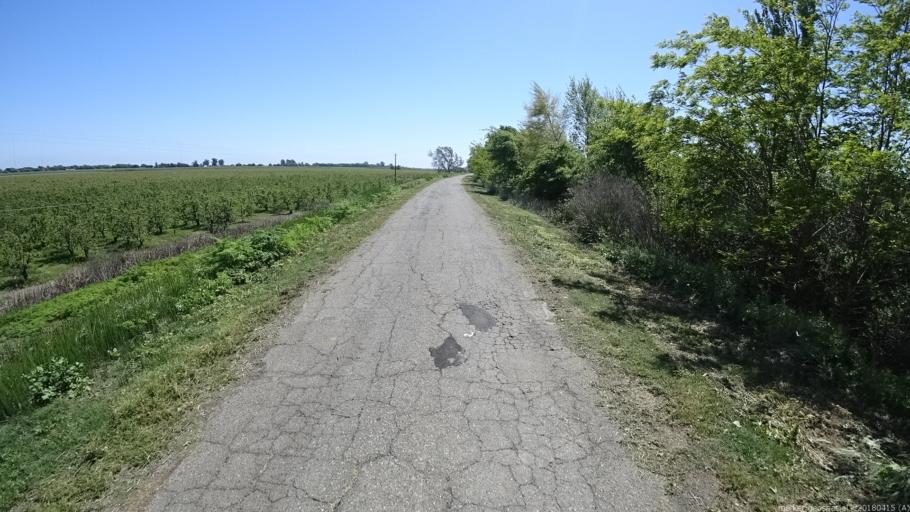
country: US
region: California
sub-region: Sacramento County
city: Walnut Grove
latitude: 38.2941
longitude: -121.6043
